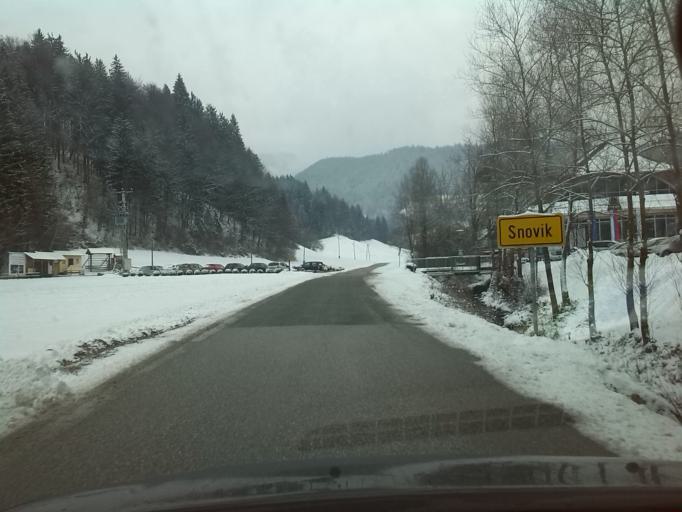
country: SI
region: Lukovica
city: Lukovica pri Domzalah
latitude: 46.2263
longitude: 14.7037
